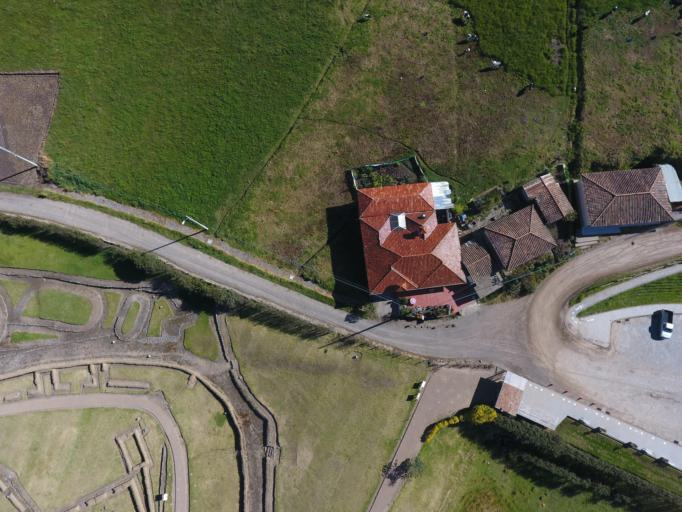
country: EC
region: Canar
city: Canar
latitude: -2.5405
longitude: -78.8729
